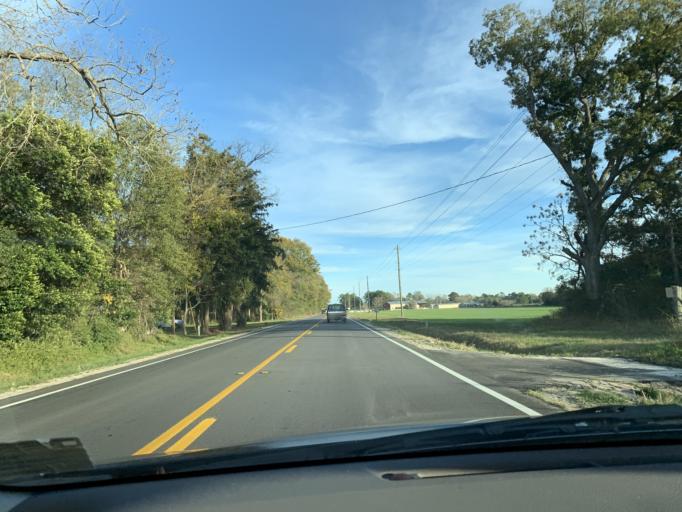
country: US
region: Georgia
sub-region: Irwin County
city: Ocilla
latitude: 31.5921
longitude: -83.1011
